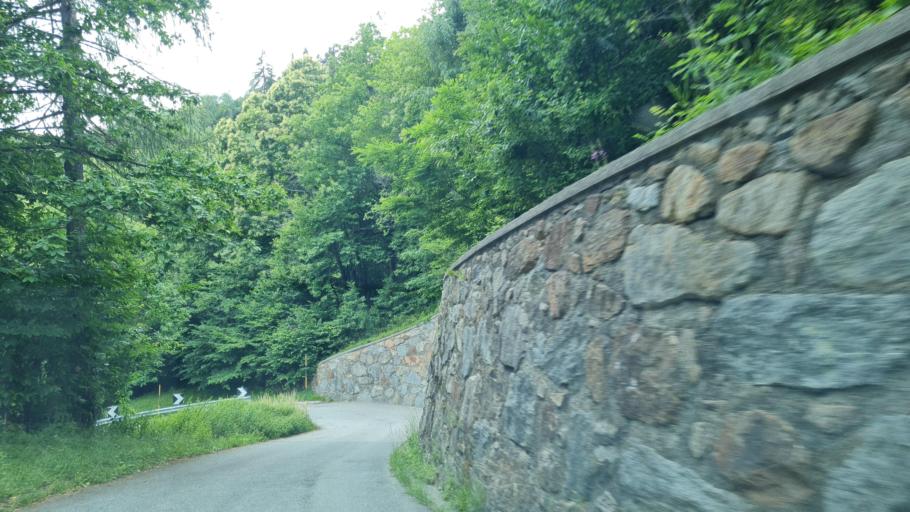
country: IT
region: Aosta Valley
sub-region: Valle d'Aosta
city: Fontainemore
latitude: 45.6542
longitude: 7.8549
